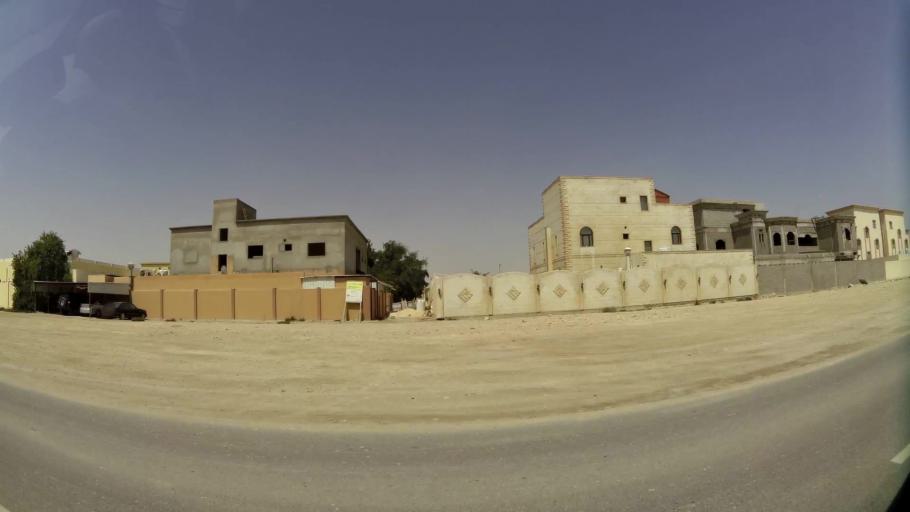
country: QA
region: Baladiyat Umm Salal
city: Umm Salal Muhammad
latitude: 25.4007
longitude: 51.4446
